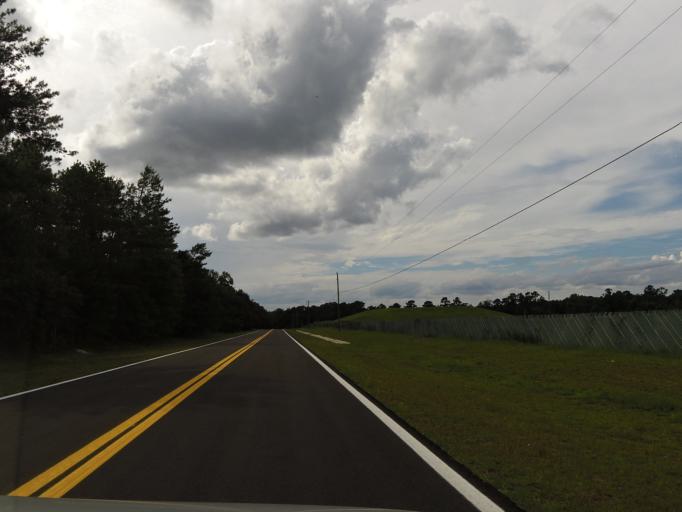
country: US
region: Florida
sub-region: Clay County
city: Green Cove Springs
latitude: 30.0041
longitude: -81.7436
